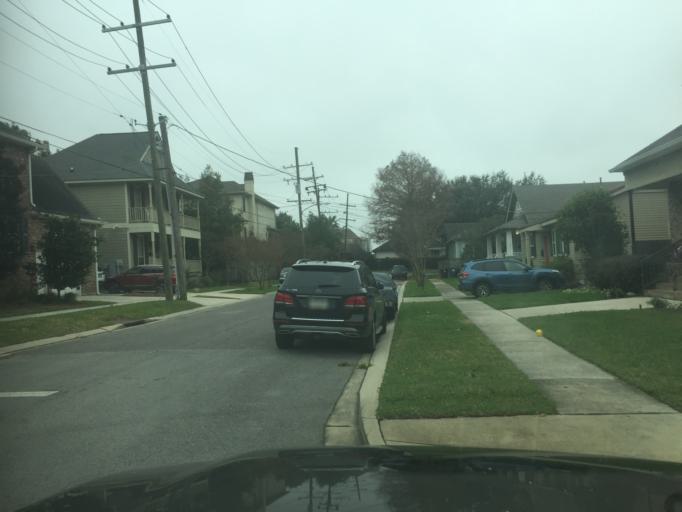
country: US
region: Louisiana
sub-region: Jefferson Parish
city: Metairie
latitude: 30.0193
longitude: -90.1125
